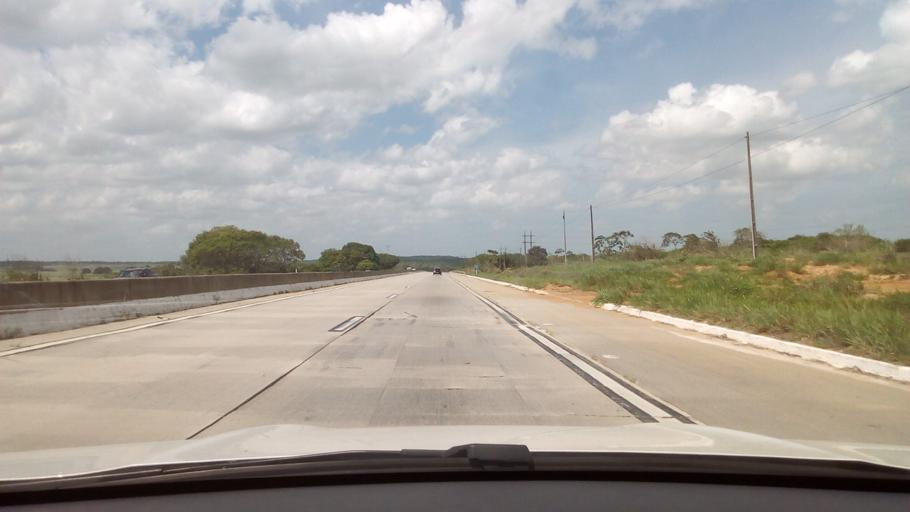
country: BR
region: Paraiba
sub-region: Rio Tinto
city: Rio Tinto
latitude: -6.7779
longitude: -35.1334
